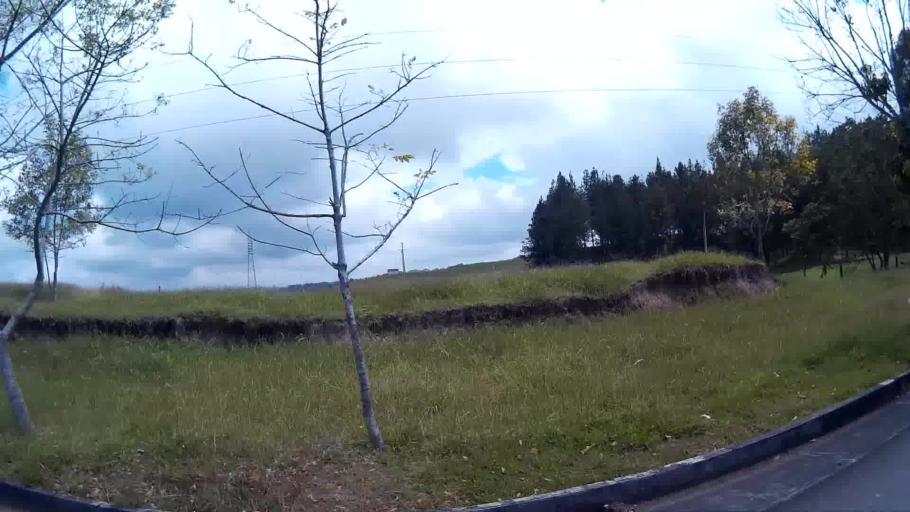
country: CO
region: Quindio
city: Salento
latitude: 4.6490
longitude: -75.6029
